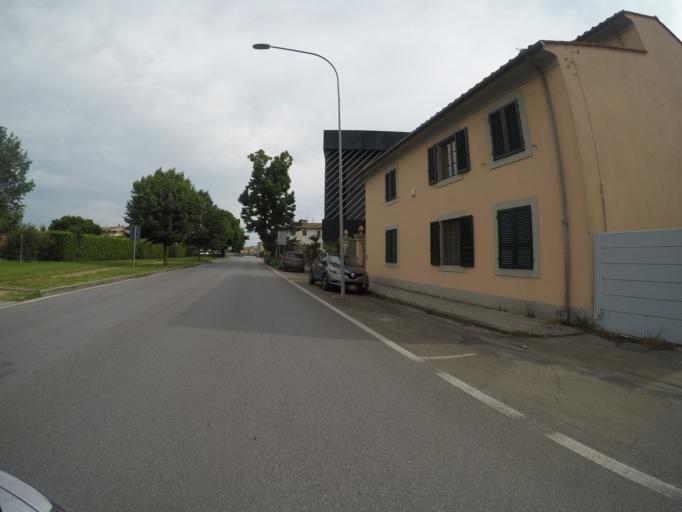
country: IT
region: Tuscany
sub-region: Province of Pisa
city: Madonna dell'Acqua
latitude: 43.7283
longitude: 10.3889
